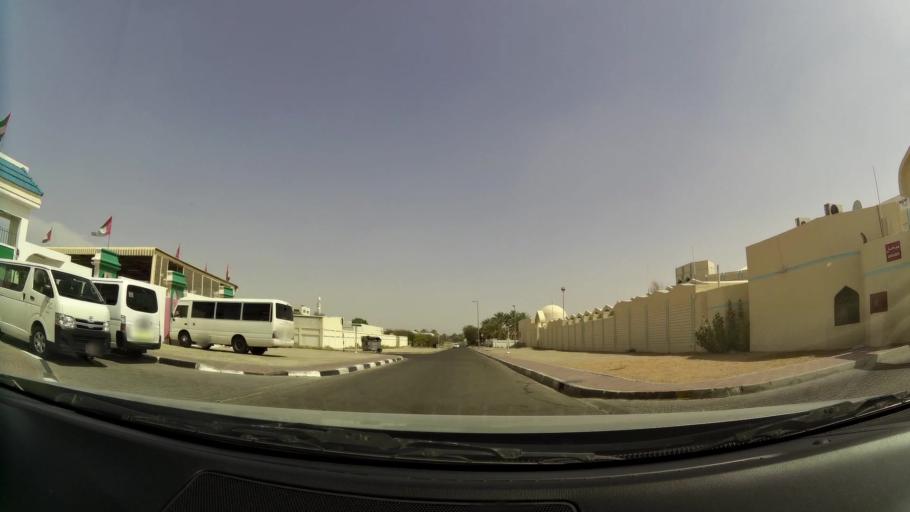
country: AE
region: Abu Dhabi
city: Al Ain
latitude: 24.2240
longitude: 55.6907
